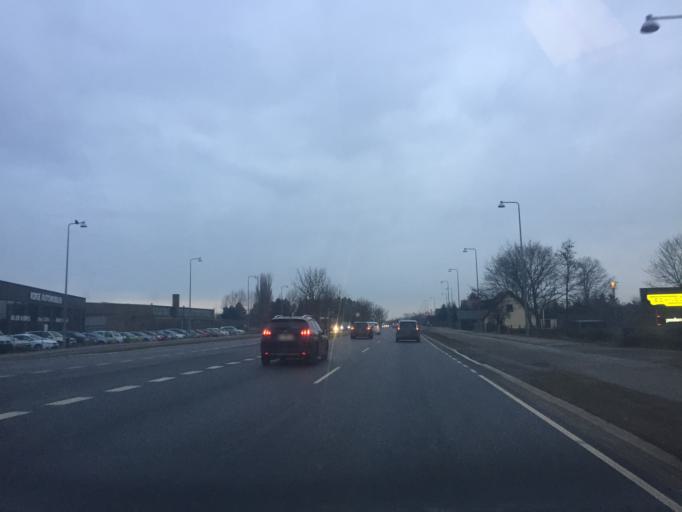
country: DK
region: Zealand
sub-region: Solrod Kommune
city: Solrod
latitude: 55.5039
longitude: 12.1991
